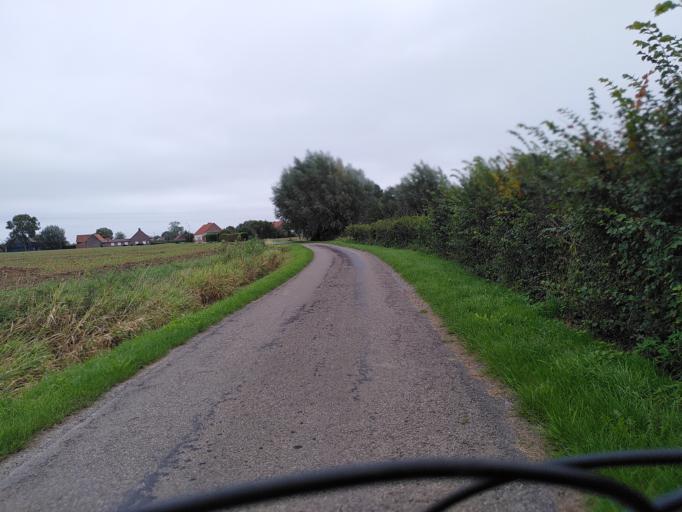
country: FR
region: Nord-Pas-de-Calais
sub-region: Departement du Pas-de-Calais
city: Guarbecque
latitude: 50.6254
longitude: 2.4975
